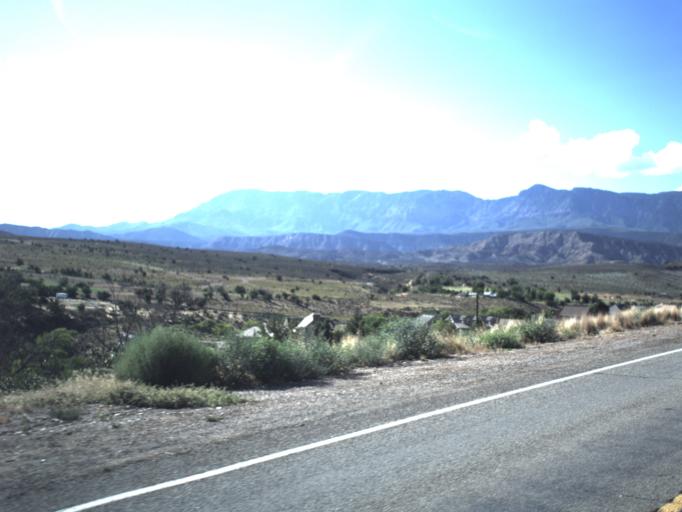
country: US
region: Utah
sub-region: Washington County
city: Toquerville
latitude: 37.2428
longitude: -113.2824
